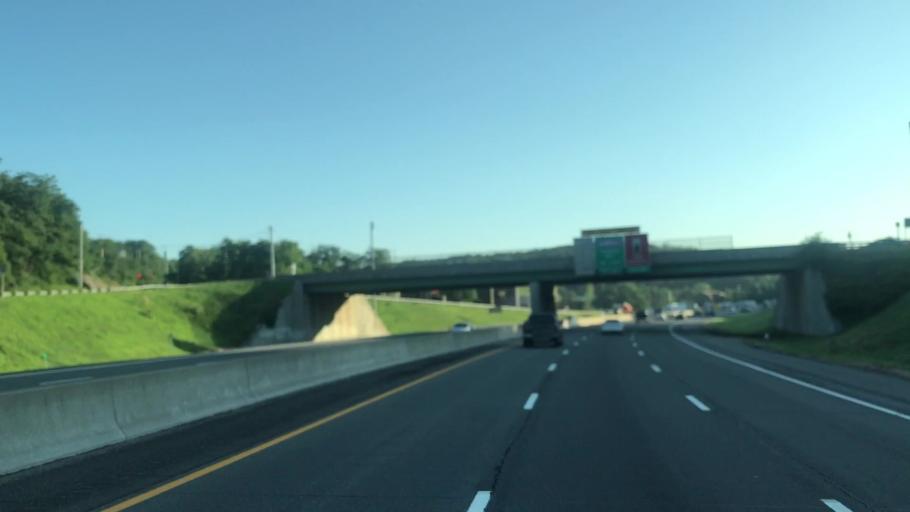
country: US
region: New York
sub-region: Westchester County
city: Hastings-on-Hudson
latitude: 40.9707
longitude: -73.8614
